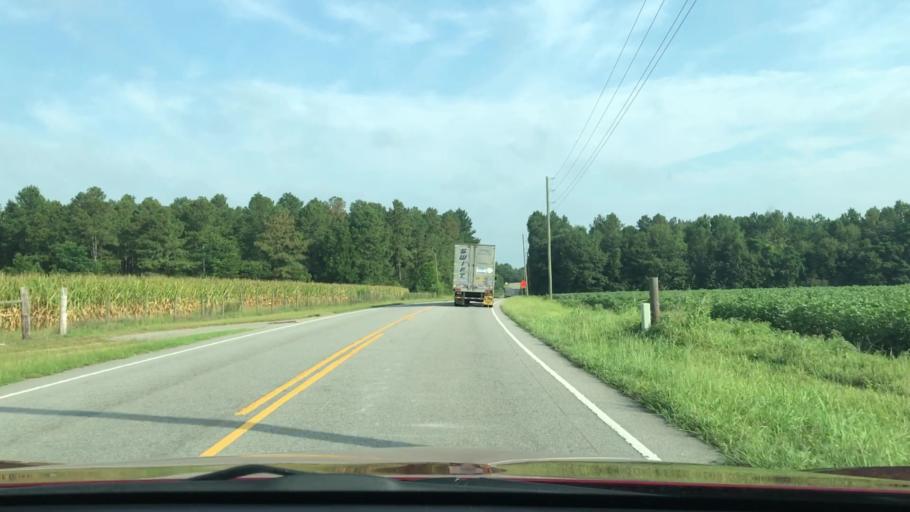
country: US
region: South Carolina
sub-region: Barnwell County
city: Blackville
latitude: 33.6006
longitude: -81.2625
